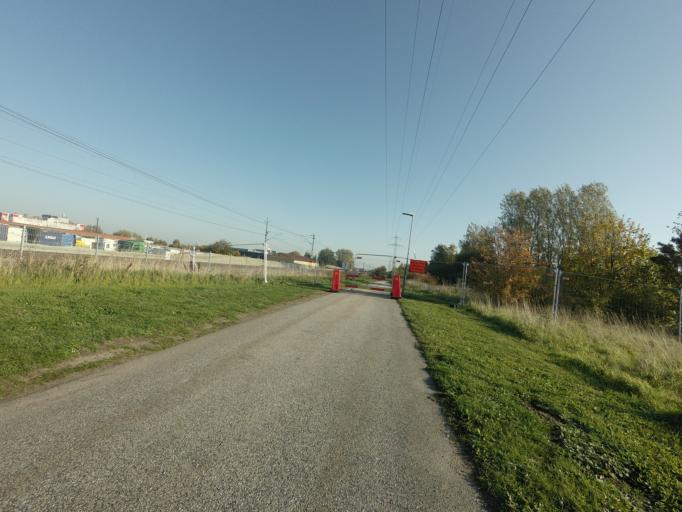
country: SE
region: Skane
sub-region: Burlovs Kommun
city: Arloev
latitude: 55.6461
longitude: 13.0895
